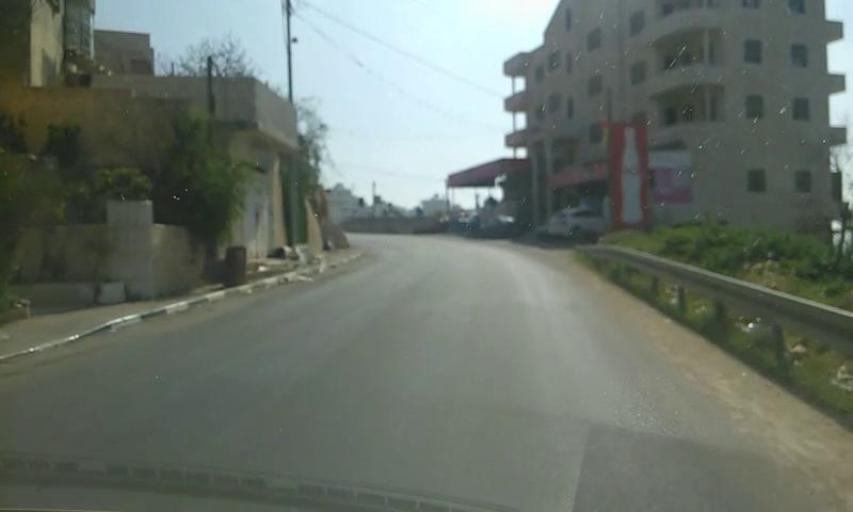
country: PS
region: West Bank
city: Dayr Jarir
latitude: 31.9707
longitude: 35.2854
